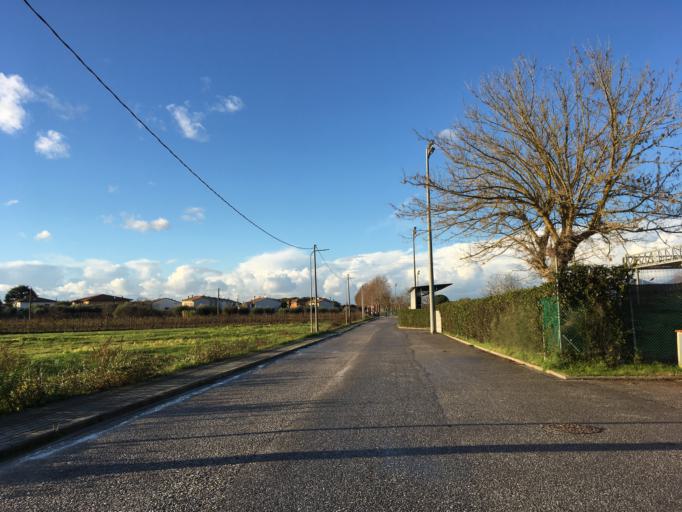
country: IT
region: Tuscany
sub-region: Province of Pisa
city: Cenaia
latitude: 43.6027
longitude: 10.5439
